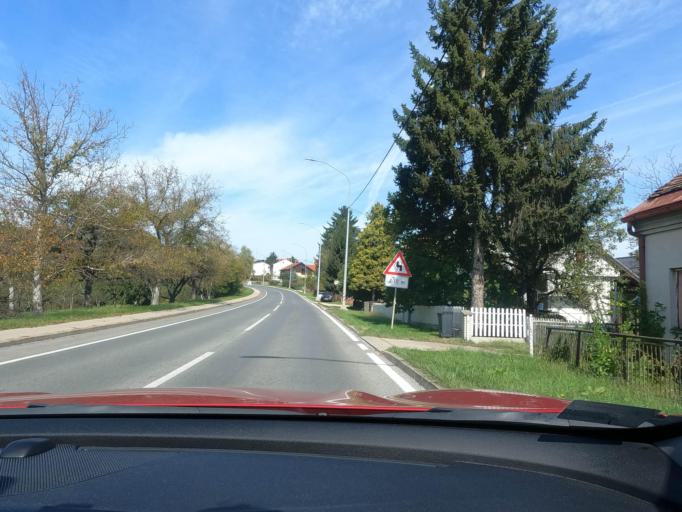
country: HR
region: Sisacko-Moslavacka
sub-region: Grad Sisak
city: Sisak
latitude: 45.4641
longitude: 16.3719
